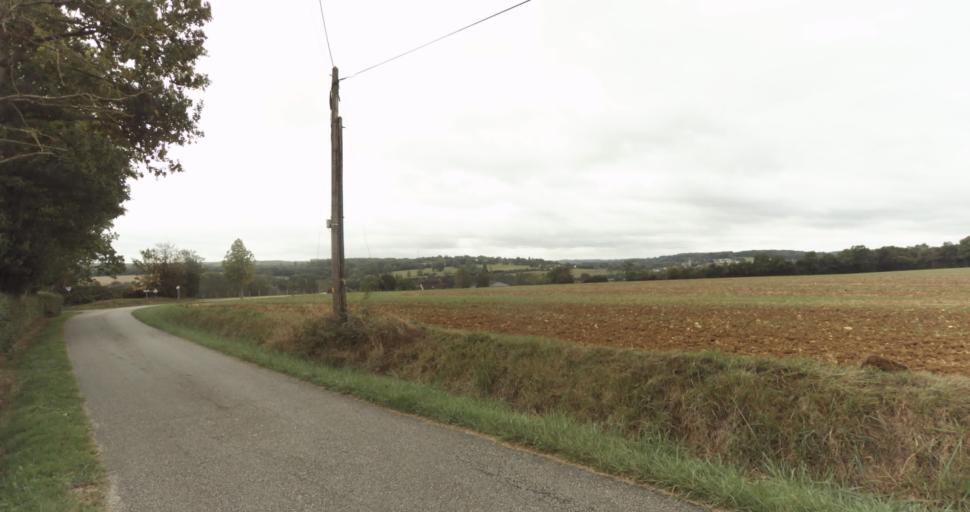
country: FR
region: Lower Normandy
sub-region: Departement de l'Orne
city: Sainte-Gauburge-Sainte-Colombe
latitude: 48.7269
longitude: 0.4406
